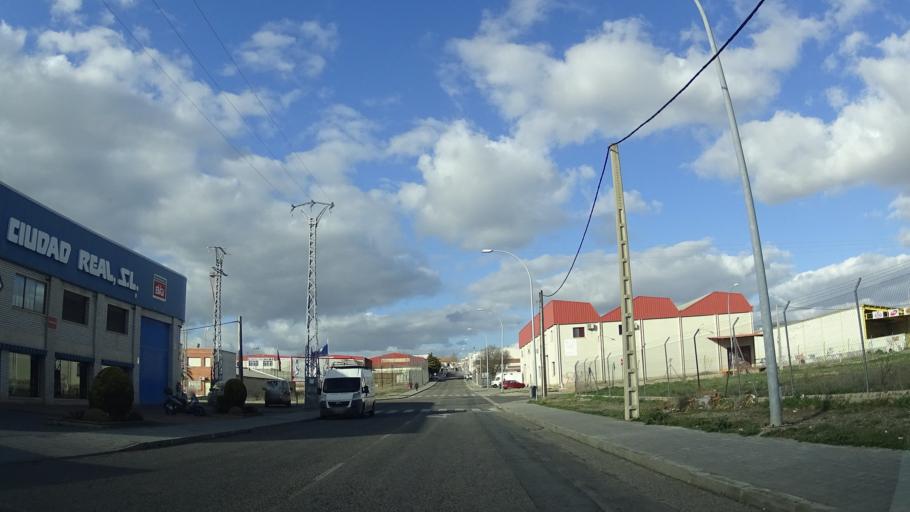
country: ES
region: Castille-La Mancha
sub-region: Provincia de Ciudad Real
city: Ciudad Real
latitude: 38.9747
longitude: -3.9315
